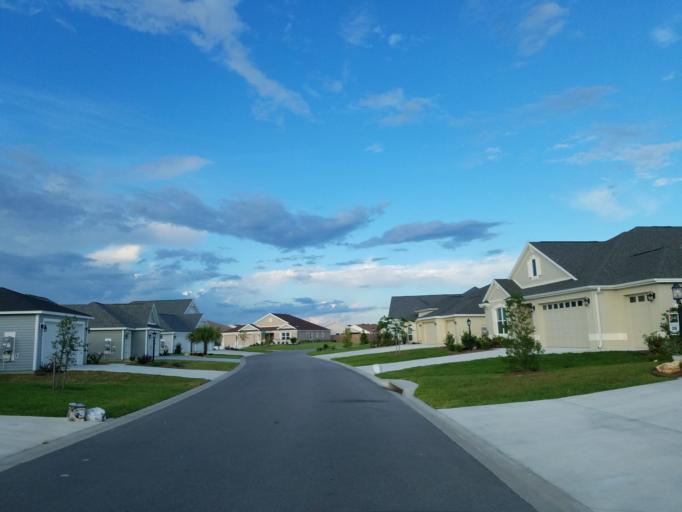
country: US
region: Florida
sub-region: Sumter County
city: Wildwood
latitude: 28.7953
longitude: -82.0274
